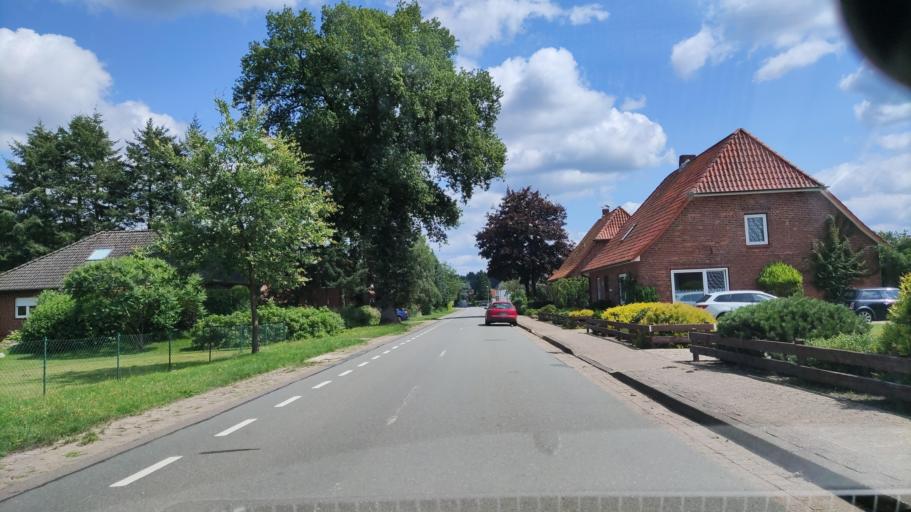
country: DE
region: Lower Saxony
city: Walsrode
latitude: 52.9067
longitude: 9.5968
